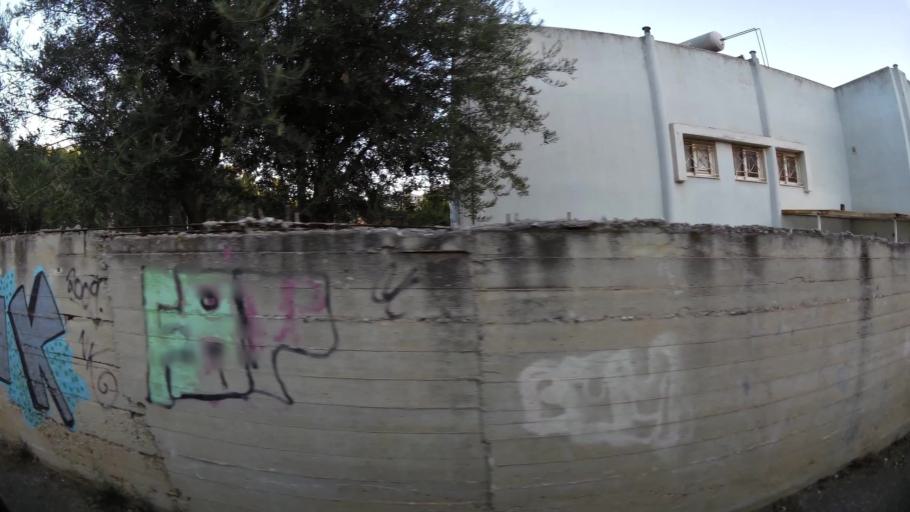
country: GR
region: Attica
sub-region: Nomarchia Anatolikis Attikis
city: Vari
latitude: 37.8228
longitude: 23.7942
